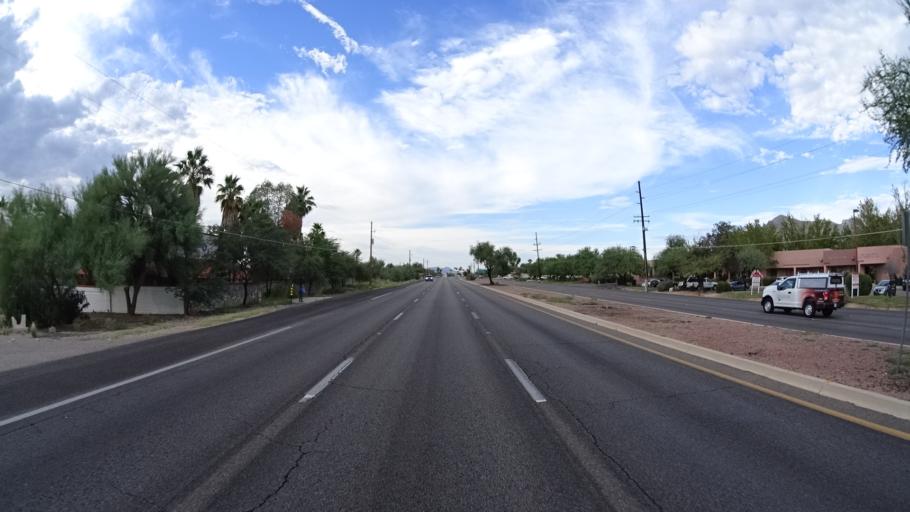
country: US
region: Arizona
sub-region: Pima County
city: Casas Adobes
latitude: 32.3283
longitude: -110.9763
